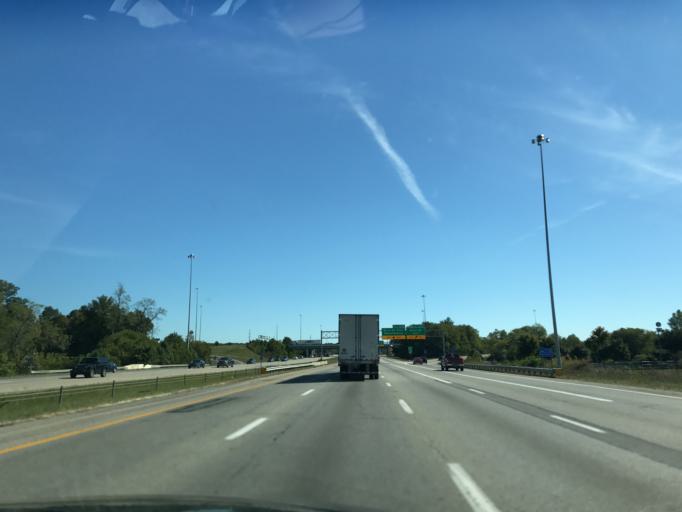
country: US
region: Ohio
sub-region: Franklin County
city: Reynoldsburg
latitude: 39.9327
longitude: -82.8358
